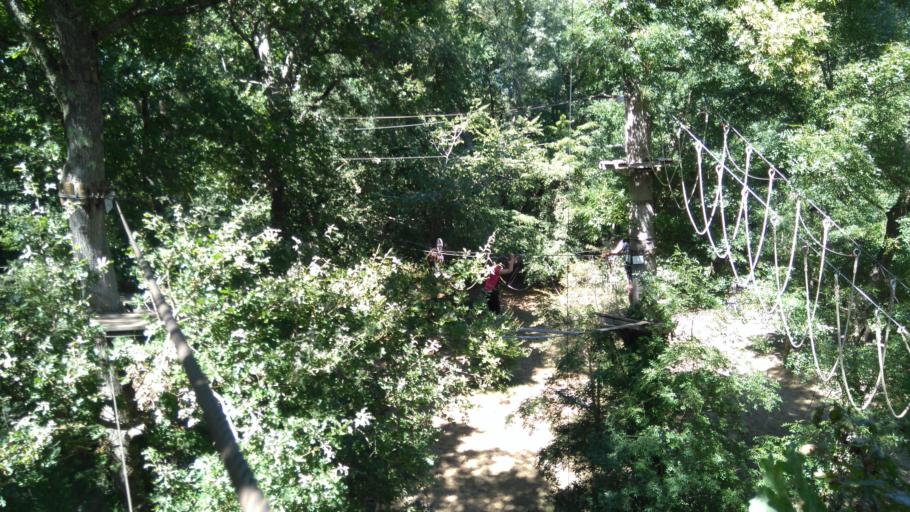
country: FR
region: Aquitaine
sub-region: Departement de la Gironde
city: Illats
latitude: 44.5477
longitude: -0.3613
